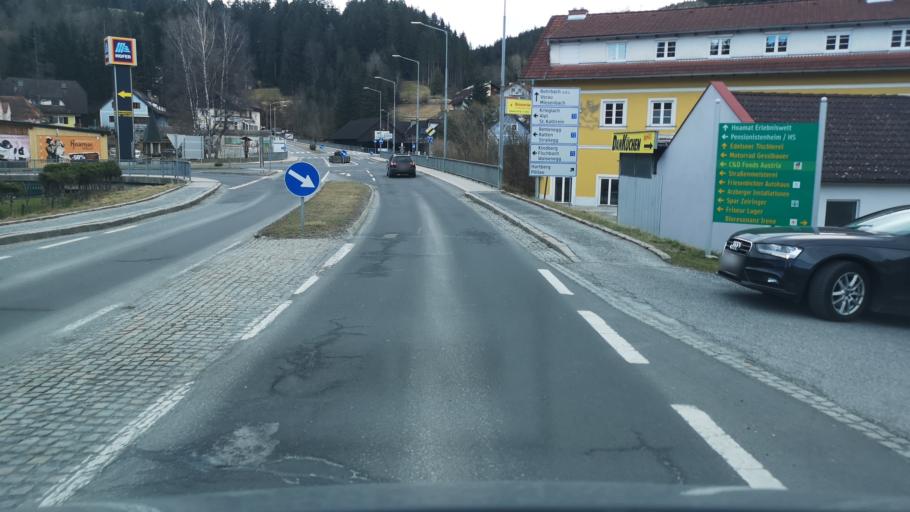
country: AT
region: Styria
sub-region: Politischer Bezirk Weiz
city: Birkfeld
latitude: 47.3536
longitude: 15.6999
